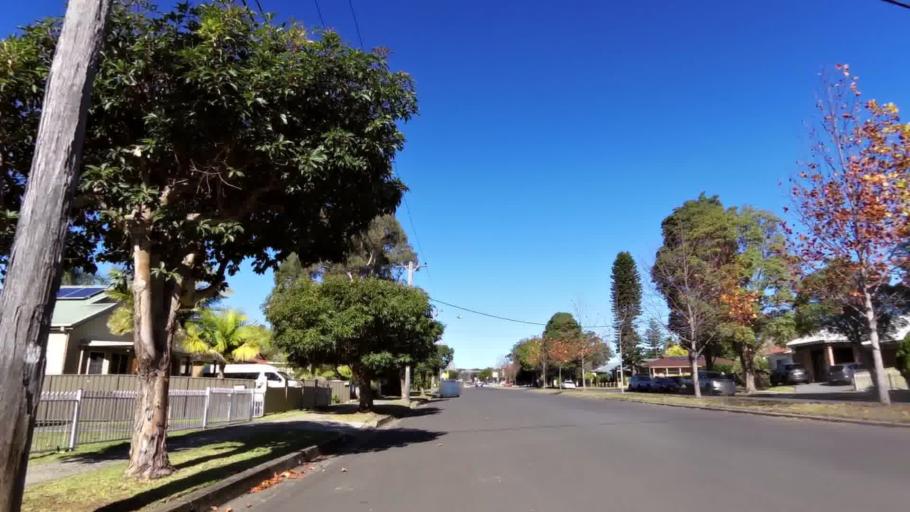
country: AU
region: New South Wales
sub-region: Shellharbour
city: Albion Park Rail
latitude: -34.5603
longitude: 150.8188
